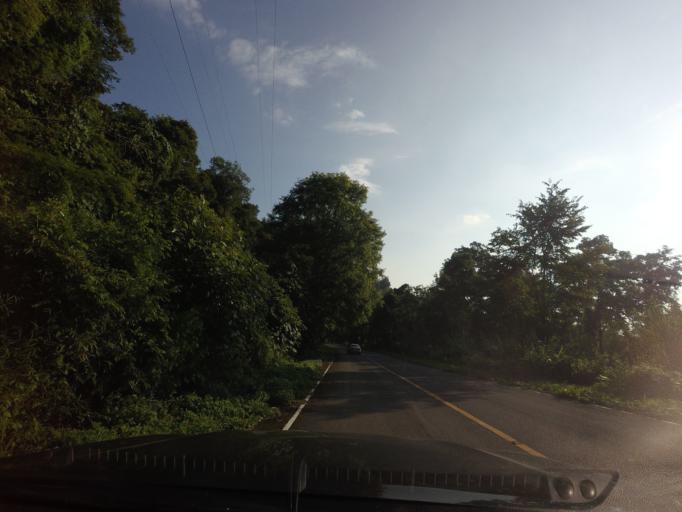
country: TH
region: Nan
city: Na Noi
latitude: 18.3656
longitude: 100.8271
